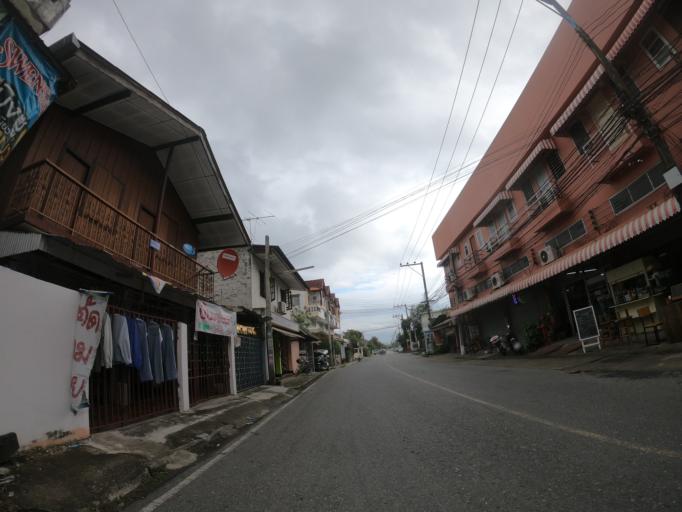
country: TH
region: Chiang Mai
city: Chiang Mai
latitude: 18.7522
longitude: 98.9707
